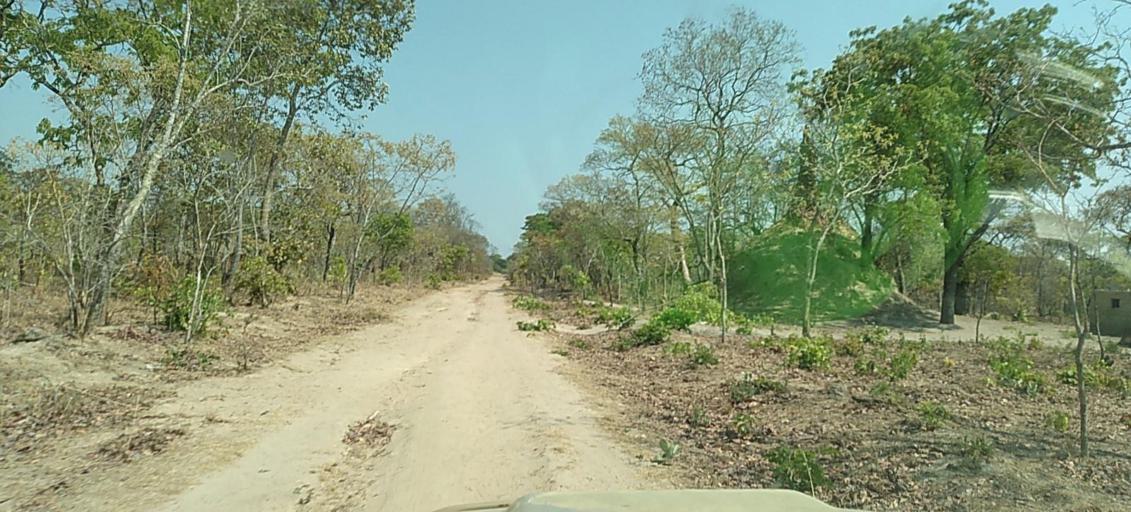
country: ZM
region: North-Western
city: Kalengwa
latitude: -13.2982
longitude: 24.7927
